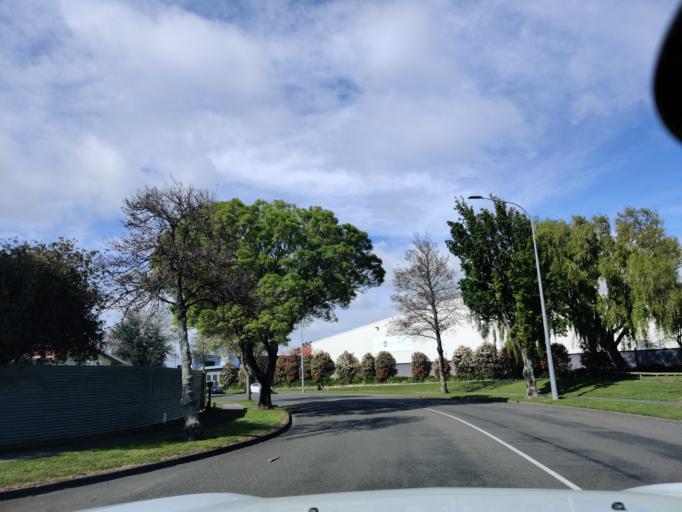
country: NZ
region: Manawatu-Wanganui
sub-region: Palmerston North City
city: Palmerston North
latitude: -40.3329
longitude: 175.6414
